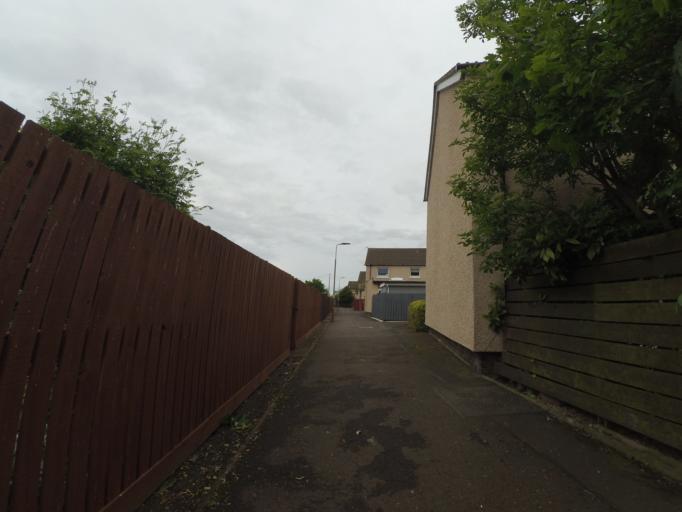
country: GB
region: Scotland
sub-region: East Lothian
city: Macmerry
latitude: 55.9396
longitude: -2.9087
